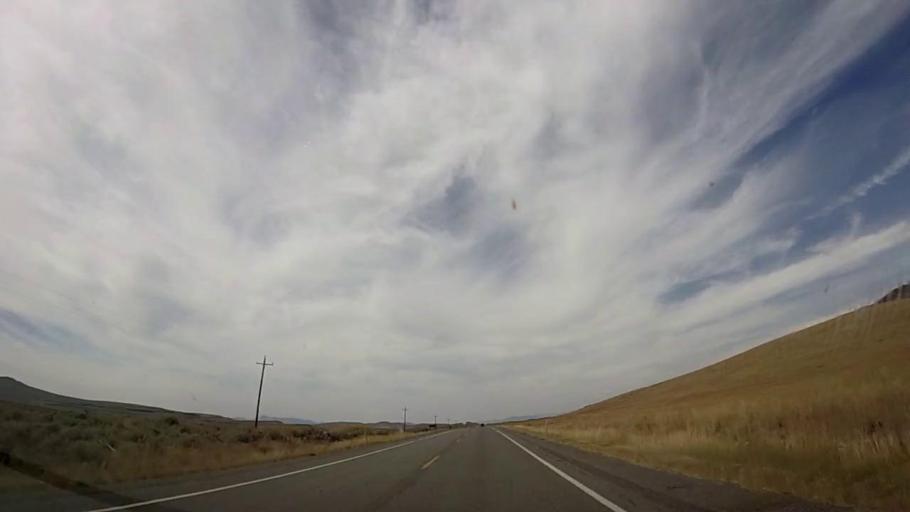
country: US
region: Idaho
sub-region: Blaine County
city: Bellevue
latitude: 43.2351
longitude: -114.3120
